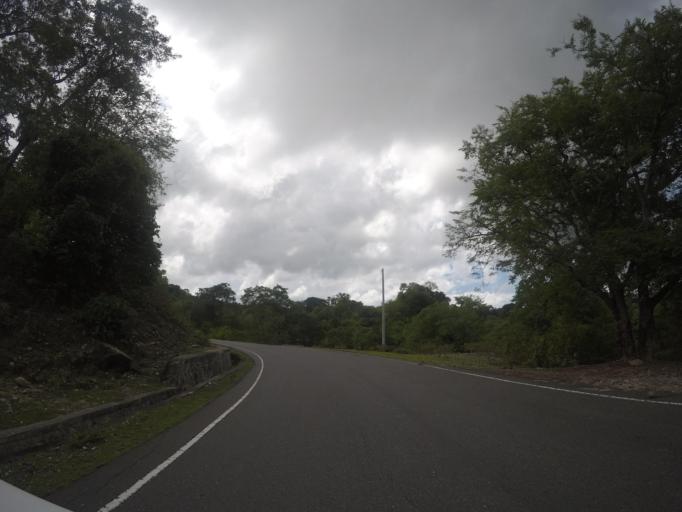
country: TL
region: Bobonaro
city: Maliana
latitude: -8.9526
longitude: 125.0858
